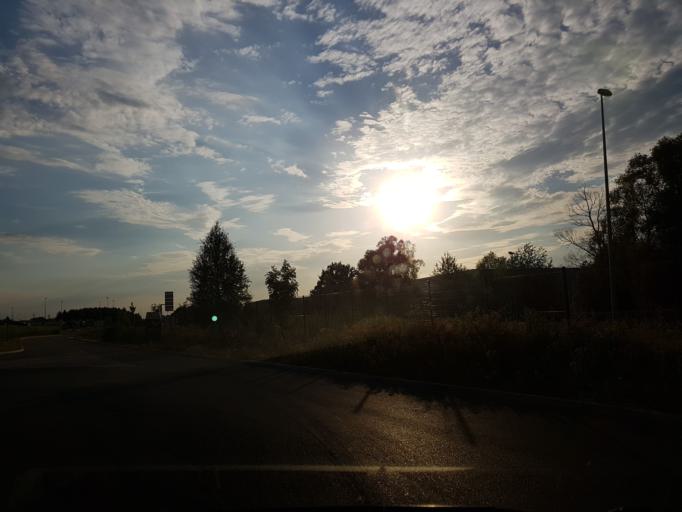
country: FR
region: Picardie
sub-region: Departement de l'Oise
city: Chevrieres
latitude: 49.3221
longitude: 2.6976
